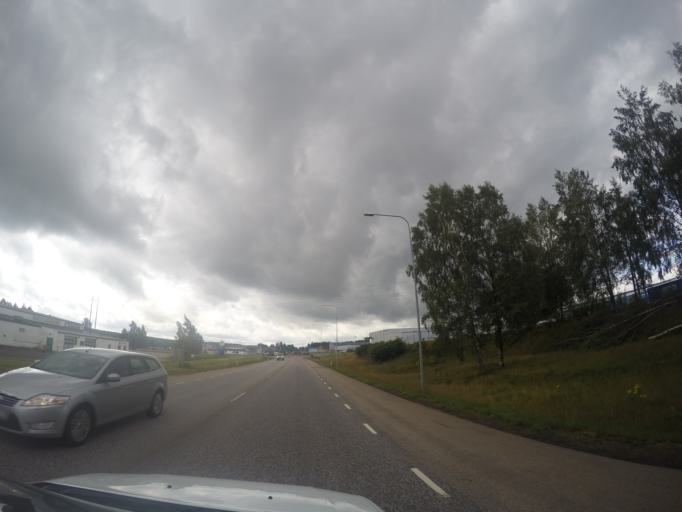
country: SE
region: Kronoberg
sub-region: Ljungby Kommun
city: Ljungby
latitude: 56.8195
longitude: 13.9178
